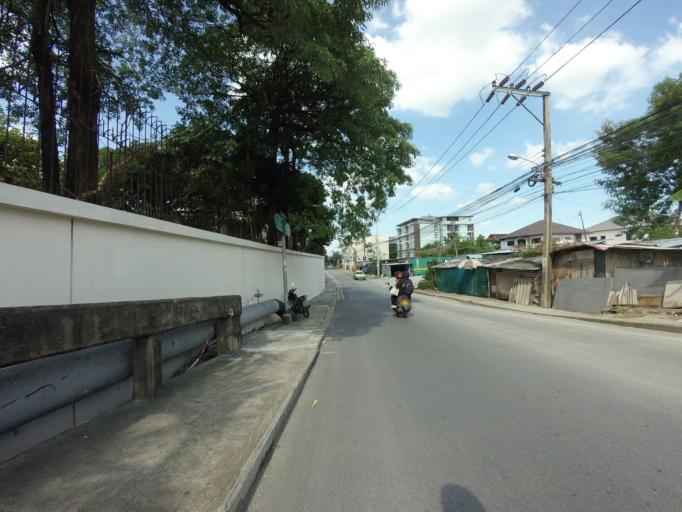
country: TH
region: Bangkok
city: Huai Khwang
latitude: 13.7889
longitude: 100.5902
